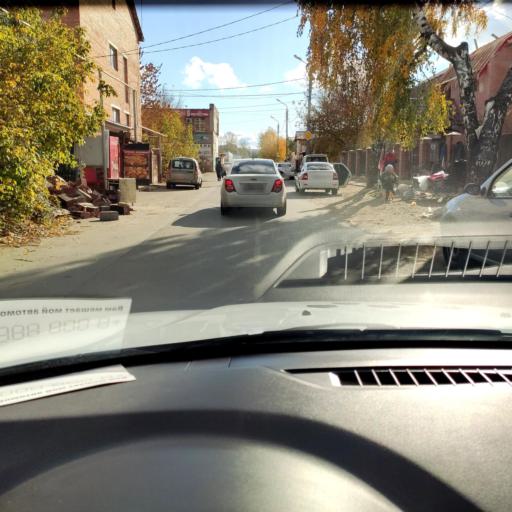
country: RU
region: Samara
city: Tol'yatti
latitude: 53.5188
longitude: 49.4078
